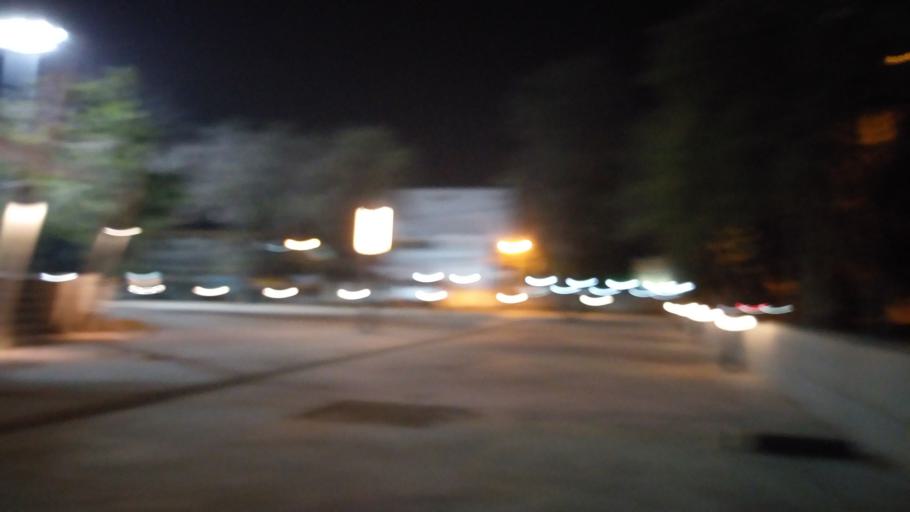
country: TH
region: Khon Kaen
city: Khon Kaen
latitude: 16.4403
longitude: 102.8355
